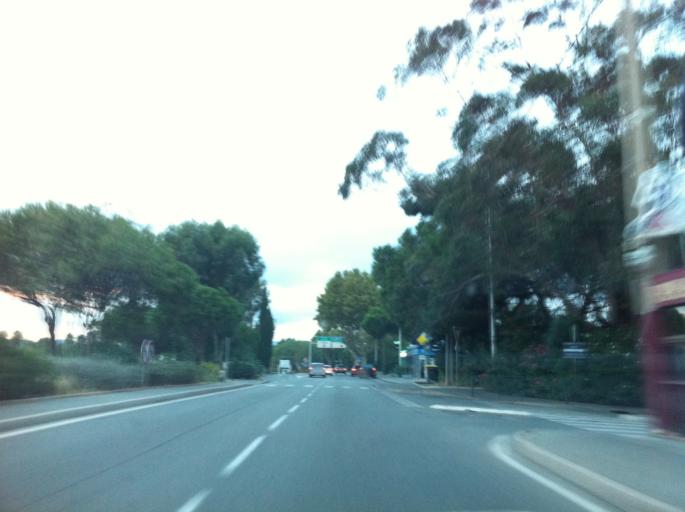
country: FR
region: Provence-Alpes-Cote d'Azur
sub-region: Departement du Var
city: Gassin
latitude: 43.2632
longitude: 6.5813
